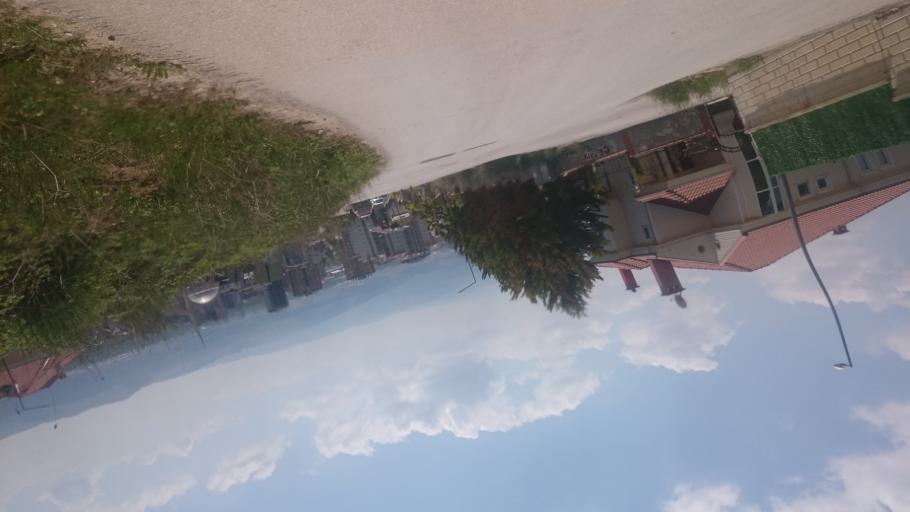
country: TR
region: Bursa
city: Gorukle
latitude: 40.2244
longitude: 28.8947
